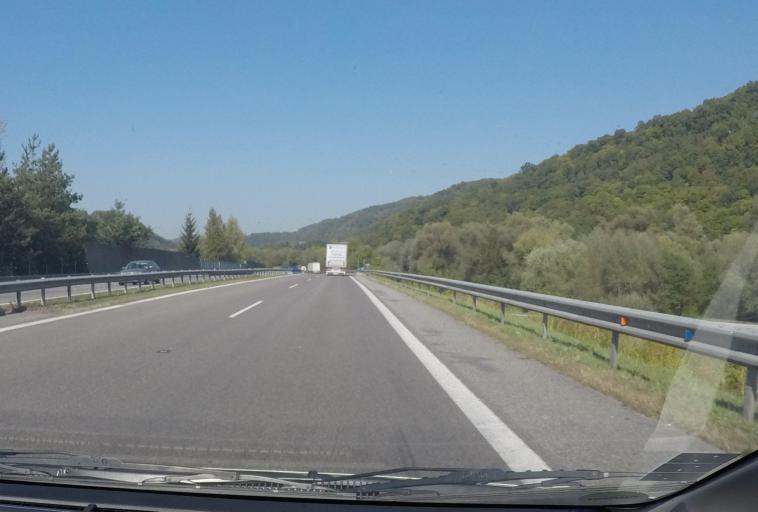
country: SK
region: Banskobystricky
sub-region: Okres Banska Bystrica
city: Zvolen
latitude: 48.5663
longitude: 19.0052
